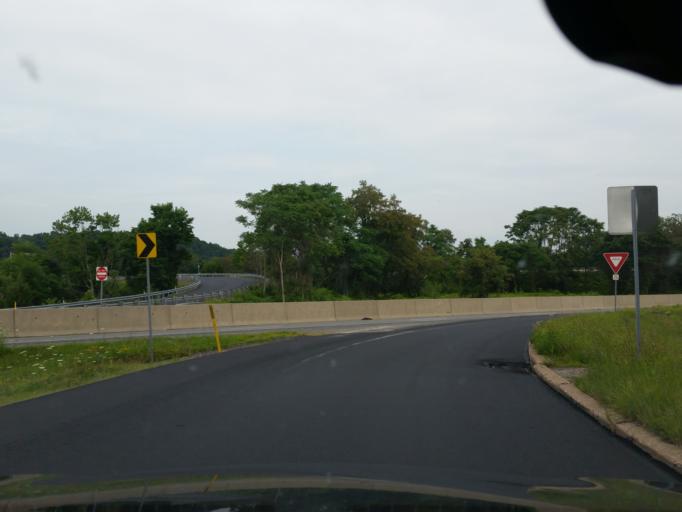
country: US
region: Pennsylvania
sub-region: Perry County
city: Duncannon
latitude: 40.4199
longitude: -77.0101
